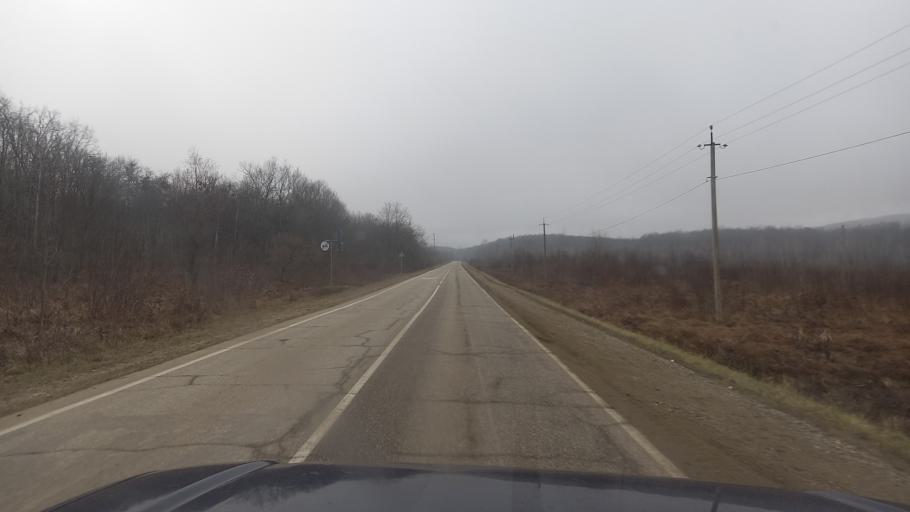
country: RU
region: Krasnodarskiy
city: Neftegorsk
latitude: 44.2891
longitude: 39.8122
